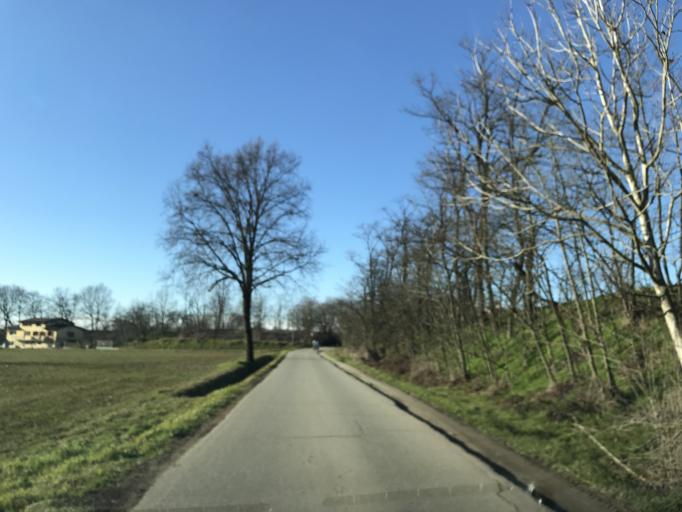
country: IT
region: Lombardy
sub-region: Provincia di Lodi
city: Bargano
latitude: 45.2338
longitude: 9.4531
